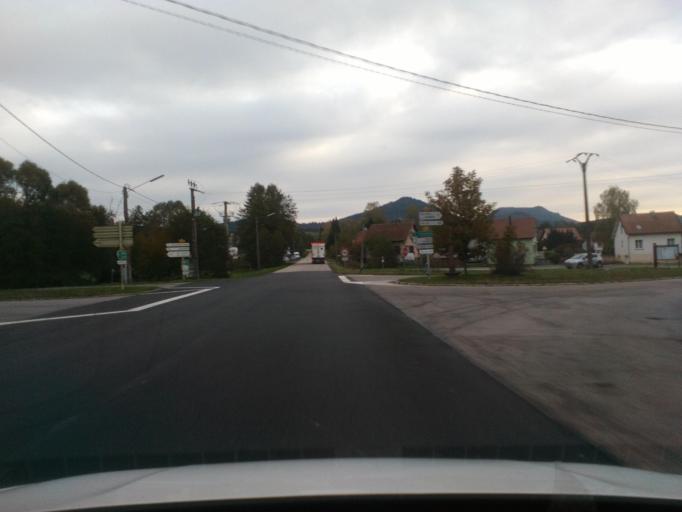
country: FR
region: Lorraine
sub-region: Departement des Vosges
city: Ban-de-Laveline
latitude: 48.3099
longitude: 7.0861
